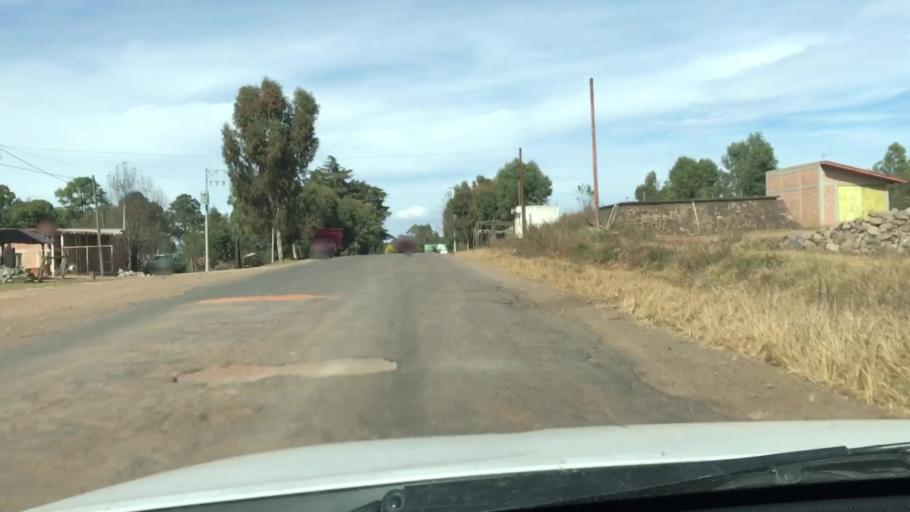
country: MX
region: Jalisco
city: Chiquilistlan
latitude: 20.1227
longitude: -103.7237
